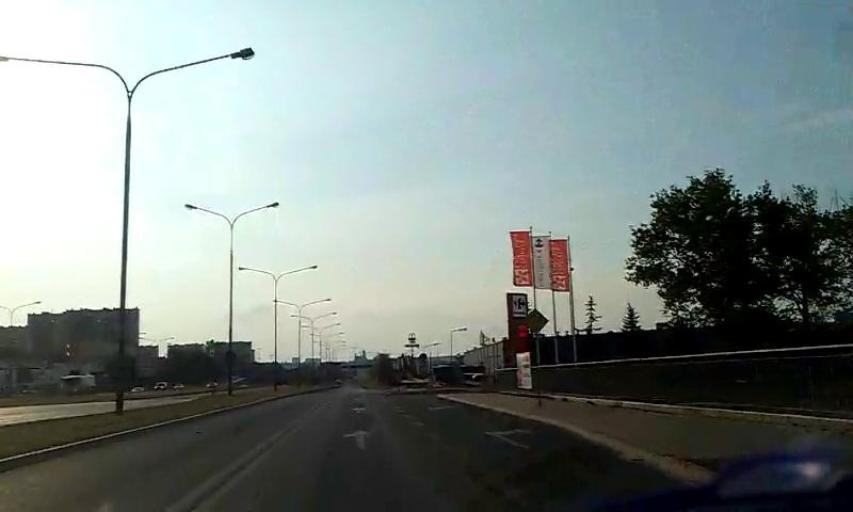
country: PL
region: Lublin Voivodeship
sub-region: Powiat lubelski
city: Lublin
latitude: 51.2345
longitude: 22.6023
